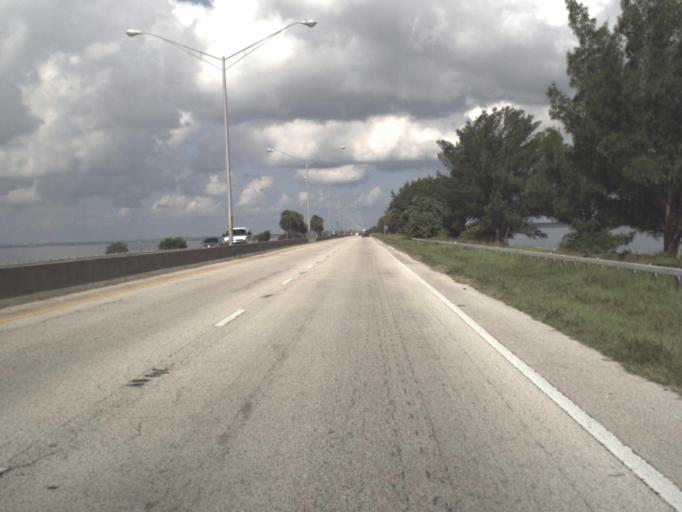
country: US
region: Florida
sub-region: Pinellas County
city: Safety Harbor
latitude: 27.9669
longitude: -82.6502
